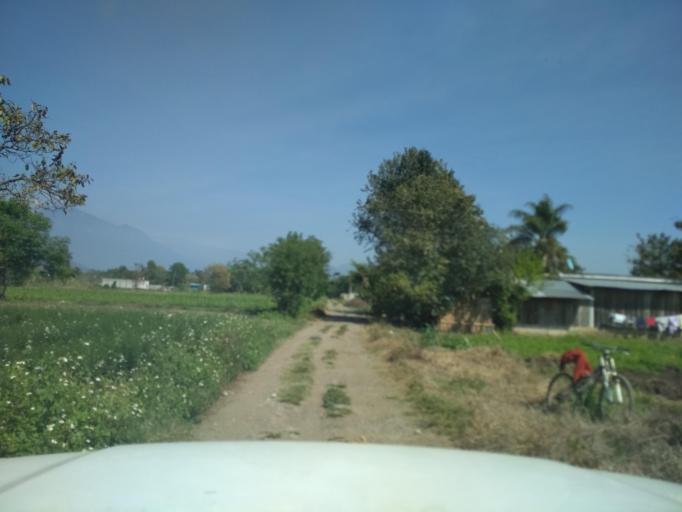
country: MX
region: Veracruz
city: Jalapilla
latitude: 18.8138
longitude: -97.0845
